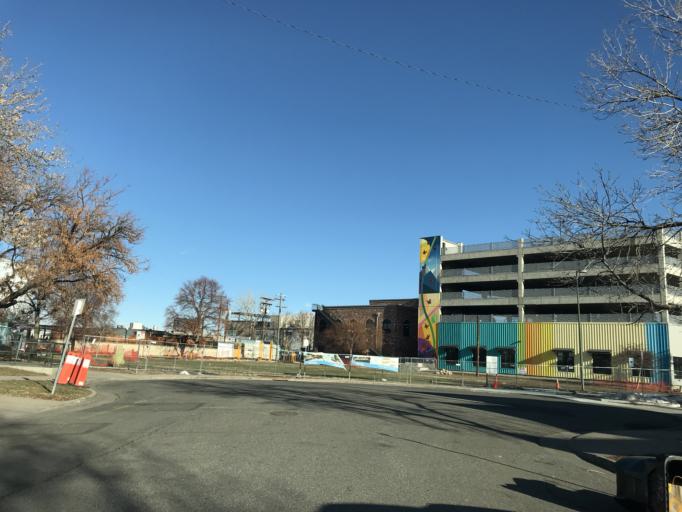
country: US
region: Colorado
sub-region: Denver County
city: Denver
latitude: 39.7691
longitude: -104.9708
